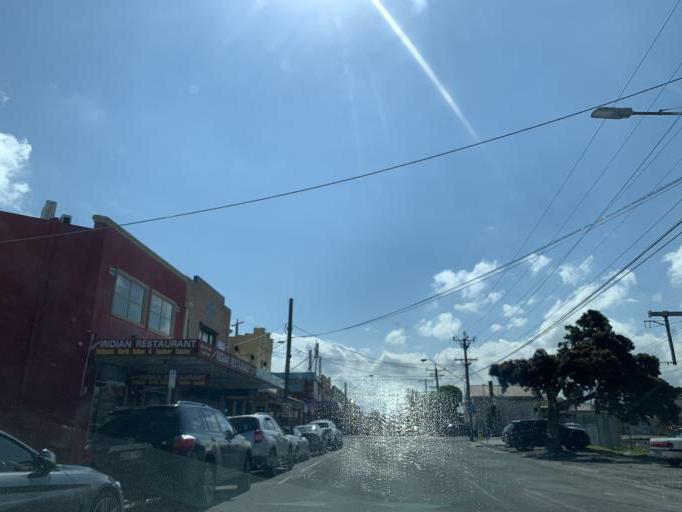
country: AU
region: Victoria
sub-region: Kingston
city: Parkdale
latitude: -37.9942
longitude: 145.0773
